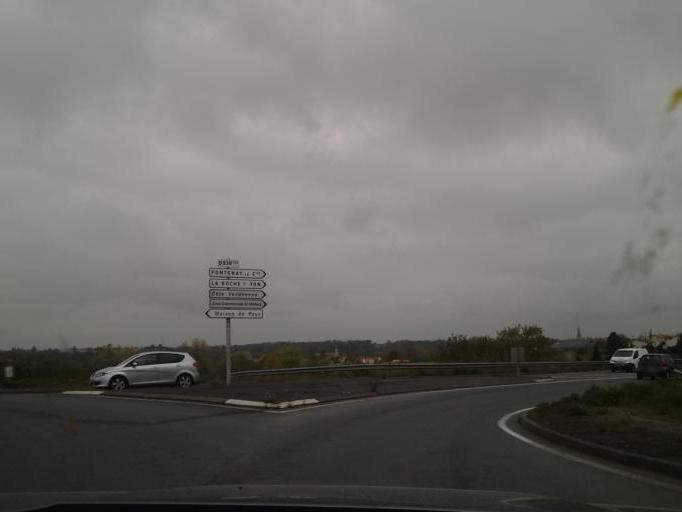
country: FR
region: Pays de la Loire
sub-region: Departement de la Vendee
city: Fontenay-le-Comte
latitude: 46.4475
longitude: -0.8127
